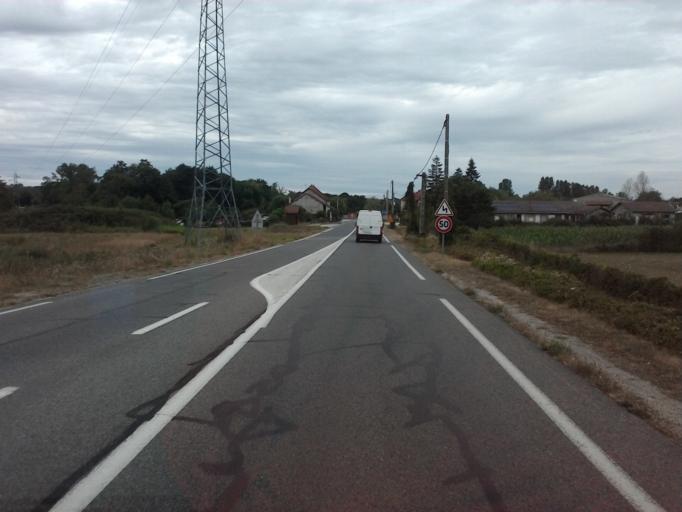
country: FR
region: Rhone-Alpes
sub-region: Departement de l'Isere
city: Sermerieu
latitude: 45.7166
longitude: 5.4241
